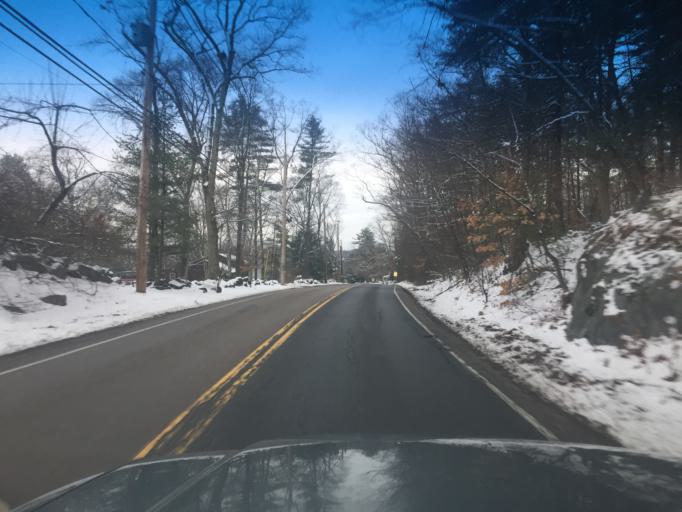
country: US
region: Massachusetts
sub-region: Middlesex County
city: Holliston
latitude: 42.1911
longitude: -71.4163
